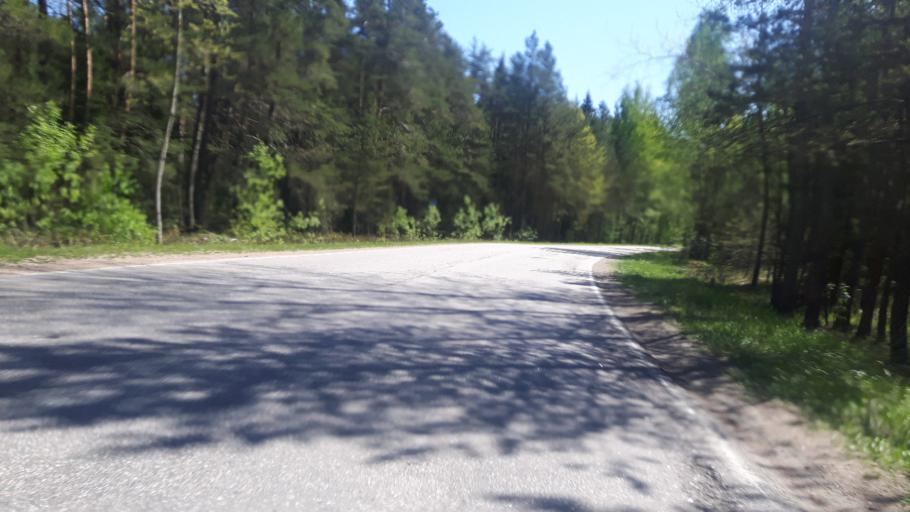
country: RU
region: Leningrad
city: Glebychevo
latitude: 60.3579
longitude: 28.8112
